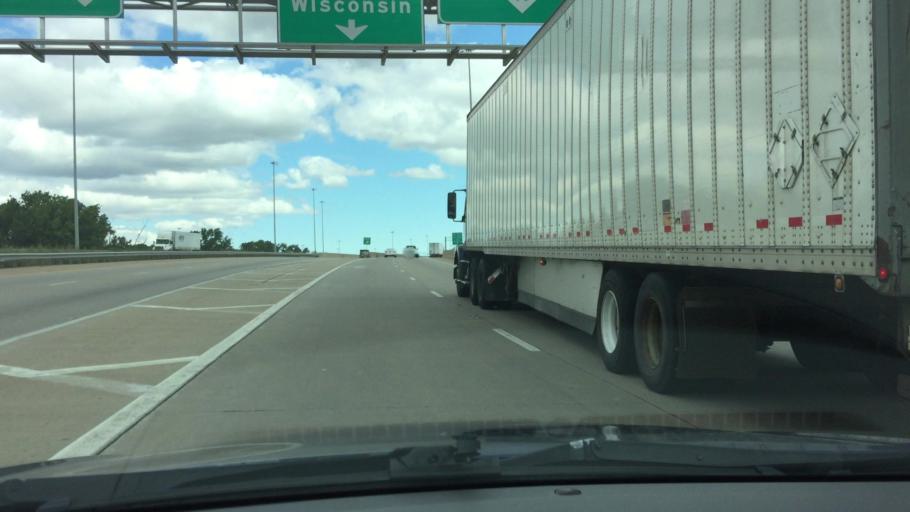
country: US
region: Illinois
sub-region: Cook County
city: Thornton
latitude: 41.5718
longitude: -87.5834
